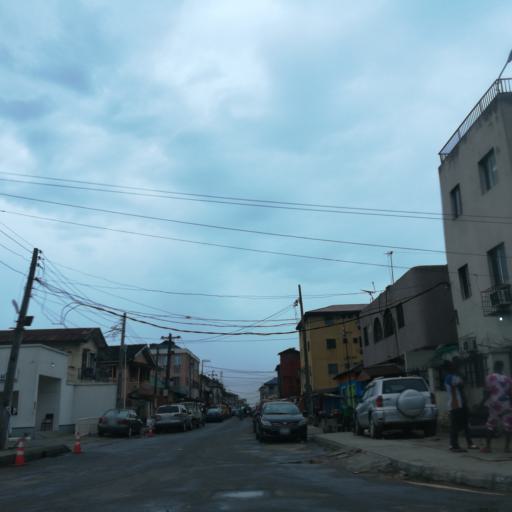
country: NG
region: Lagos
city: Ebute Metta
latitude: 6.4860
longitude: 3.3814
